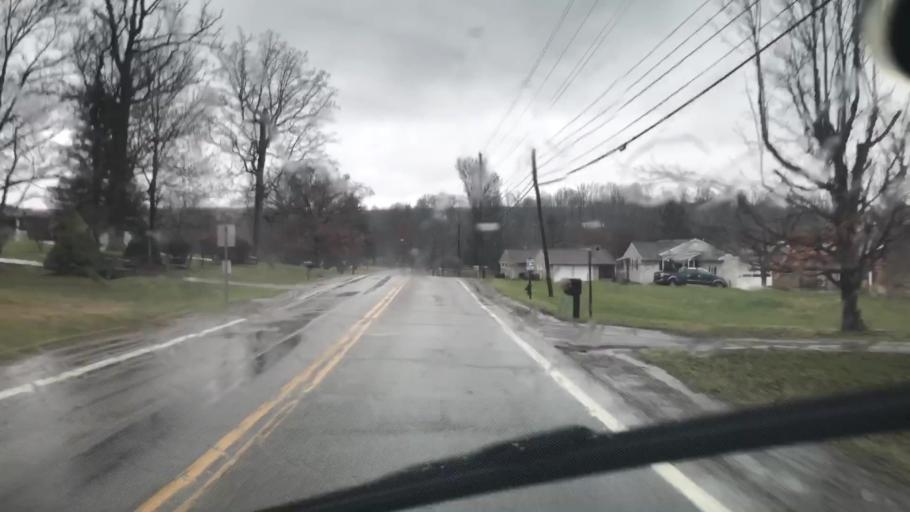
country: US
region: Ohio
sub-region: Harrison County
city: Cadiz
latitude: 40.2532
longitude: -81.0008
